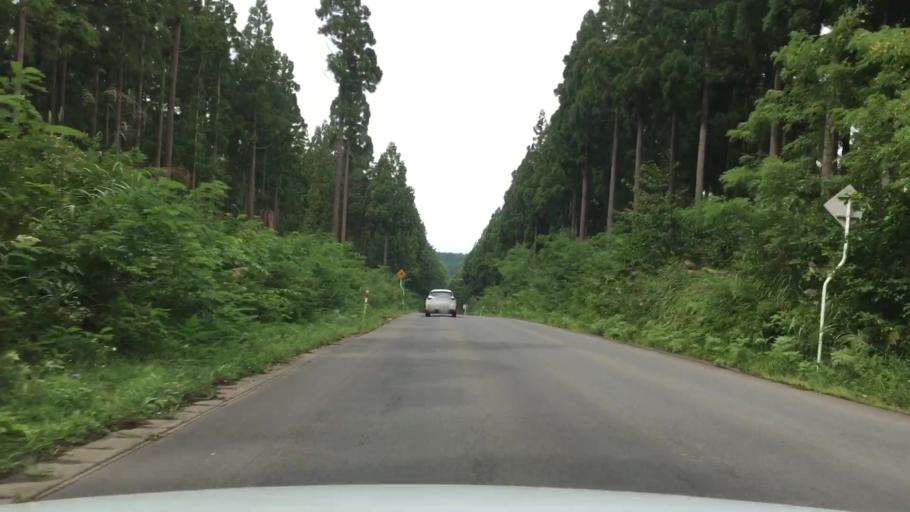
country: JP
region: Aomori
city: Shimokizukuri
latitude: 40.7114
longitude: 140.2699
